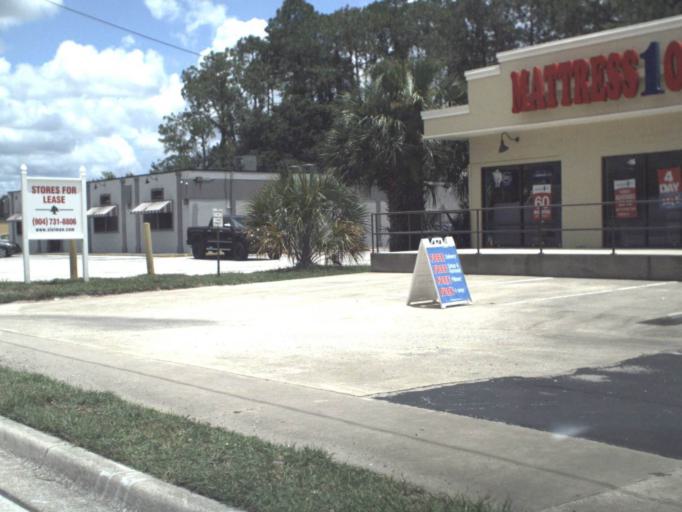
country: US
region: Florida
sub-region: Saint Johns County
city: Fruit Cove
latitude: 30.1644
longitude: -81.6324
